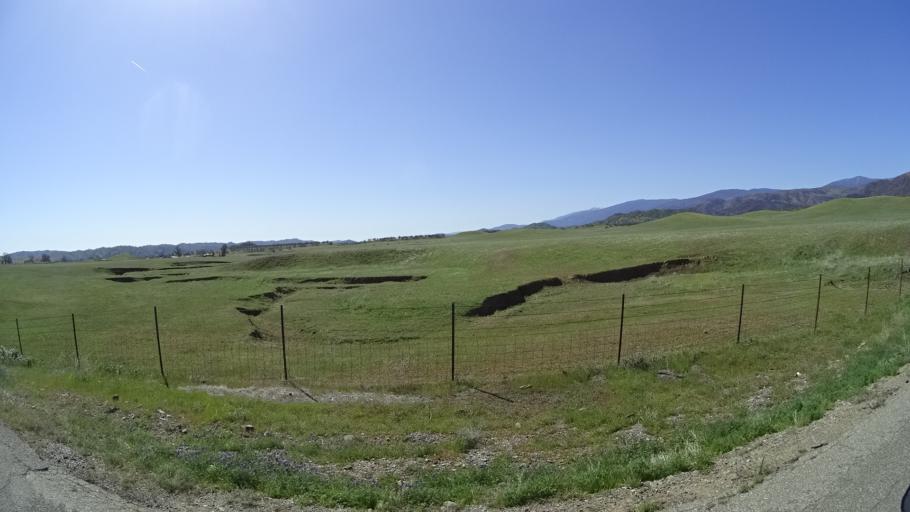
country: US
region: California
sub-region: Tehama County
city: Rancho Tehama Reserve
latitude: 39.6995
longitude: -122.5569
